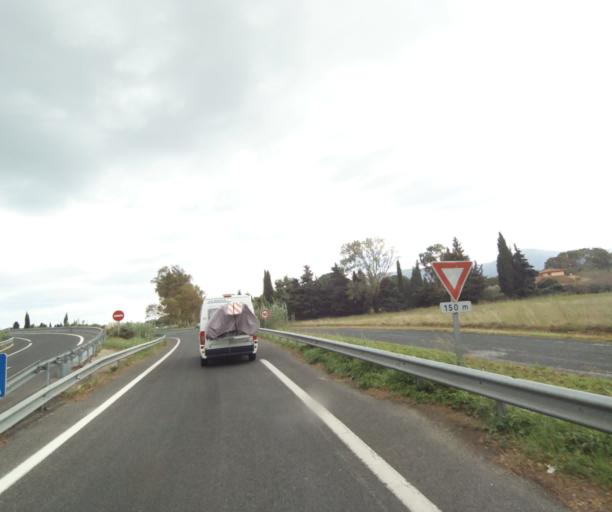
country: FR
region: Languedoc-Roussillon
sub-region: Departement des Pyrenees-Orientales
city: Elne
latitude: 42.5902
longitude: 2.9806
